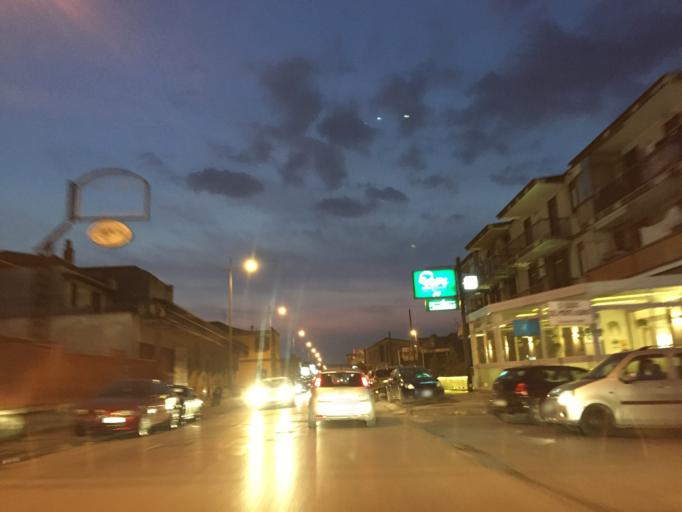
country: IT
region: Campania
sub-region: Provincia di Salerno
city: Sant'Egidio del Monte Albino
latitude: 40.7478
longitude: 14.5977
